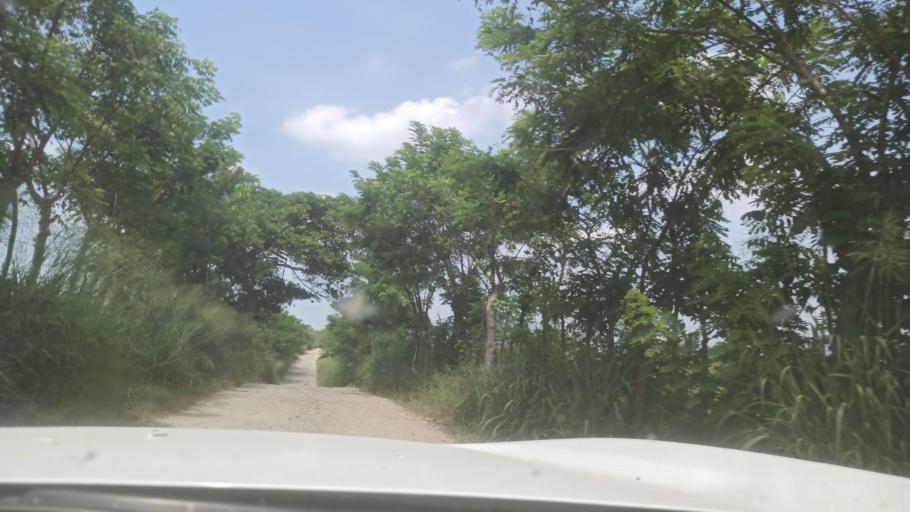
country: MX
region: Veracruz
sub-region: Atzalan
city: Colonias Pedernales
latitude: 20.0413
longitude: -97.0054
